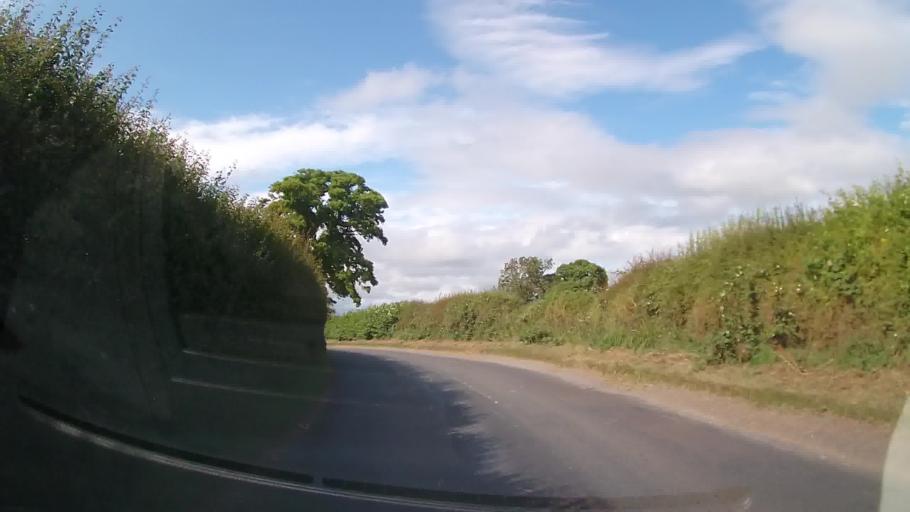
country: GB
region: England
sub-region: Shropshire
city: Petton
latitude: 52.8326
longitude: -2.8046
